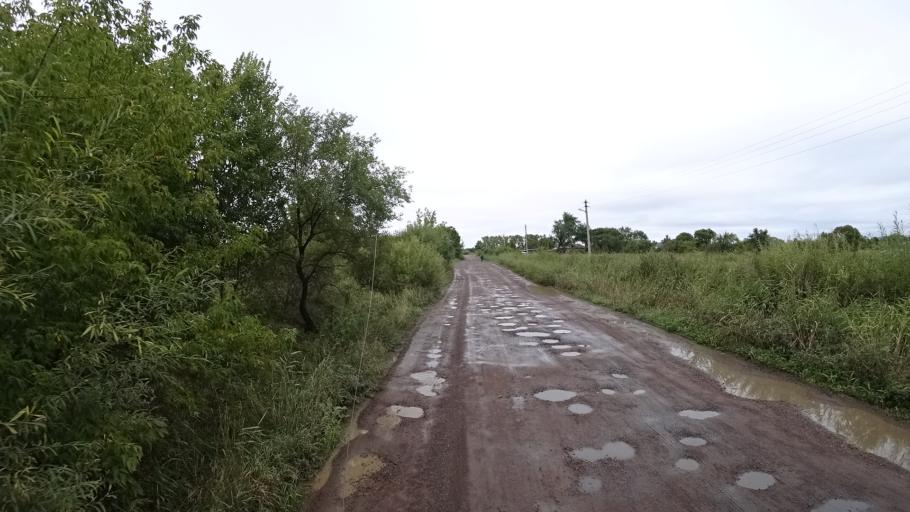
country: RU
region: Primorskiy
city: Monastyrishche
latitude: 44.1884
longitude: 132.4827
